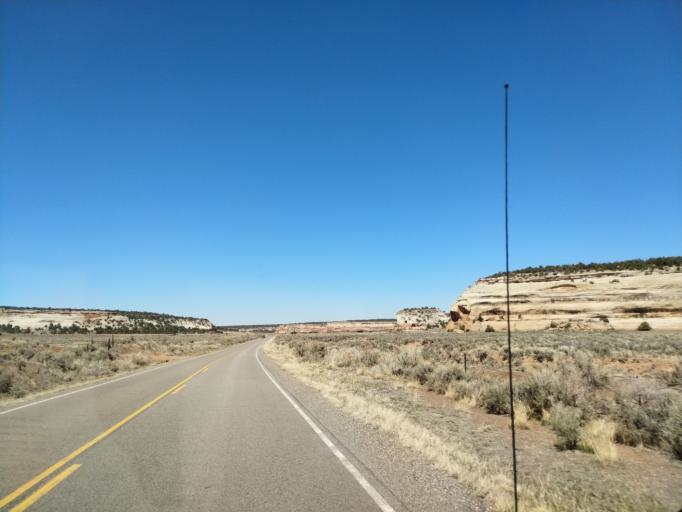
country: US
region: Colorado
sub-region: Mesa County
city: Fruita
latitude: 38.9926
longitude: -108.8212
